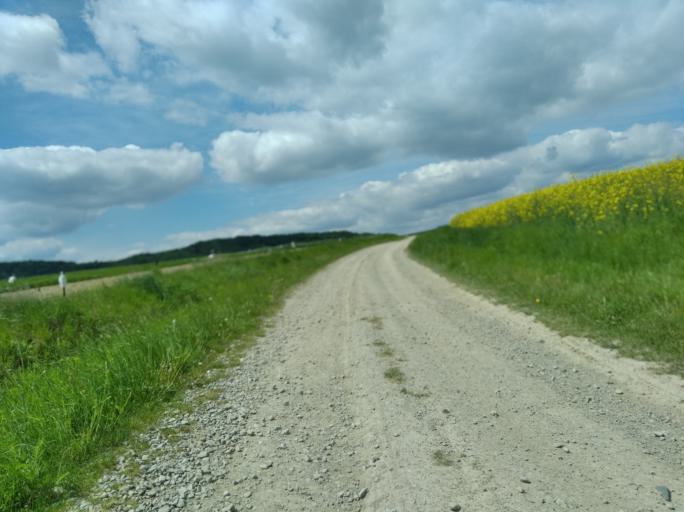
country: PL
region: Subcarpathian Voivodeship
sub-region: Powiat ropczycko-sedziszowski
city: Wielopole Skrzynskie
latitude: 49.8959
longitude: 21.5764
